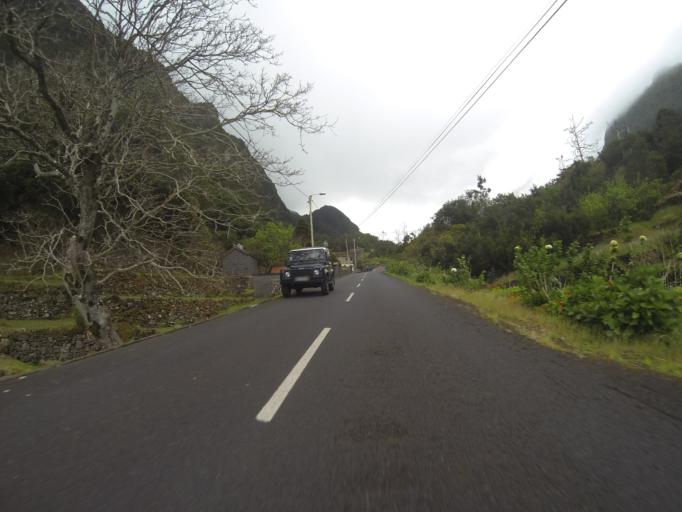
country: PT
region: Madeira
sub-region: Porto Moniz
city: Porto Moniz
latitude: 32.8155
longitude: -17.1094
